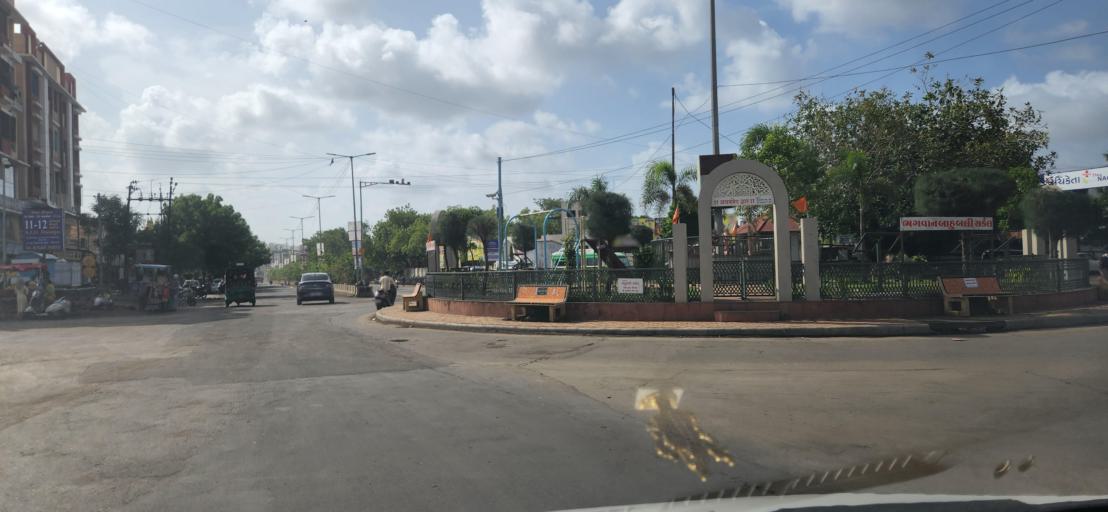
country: IN
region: Gujarat
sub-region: Bhavnagar
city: Bhavnagar
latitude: 21.7402
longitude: 72.1428
